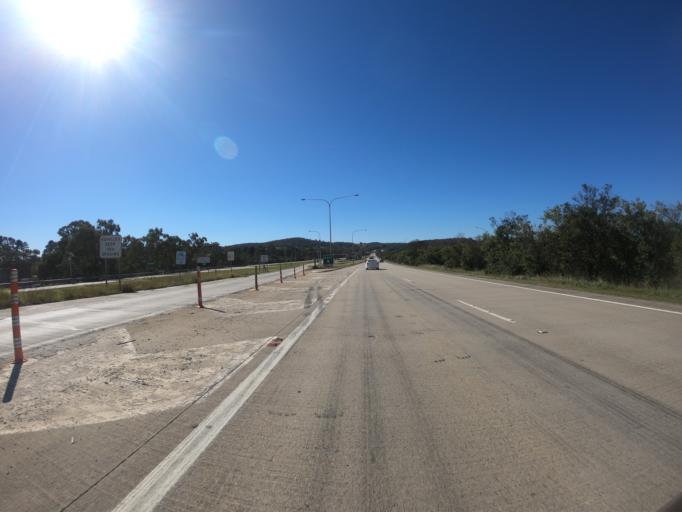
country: AU
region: New South Wales
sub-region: Wingecarribee
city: Bundanoon
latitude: -34.7067
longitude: 150.0126
